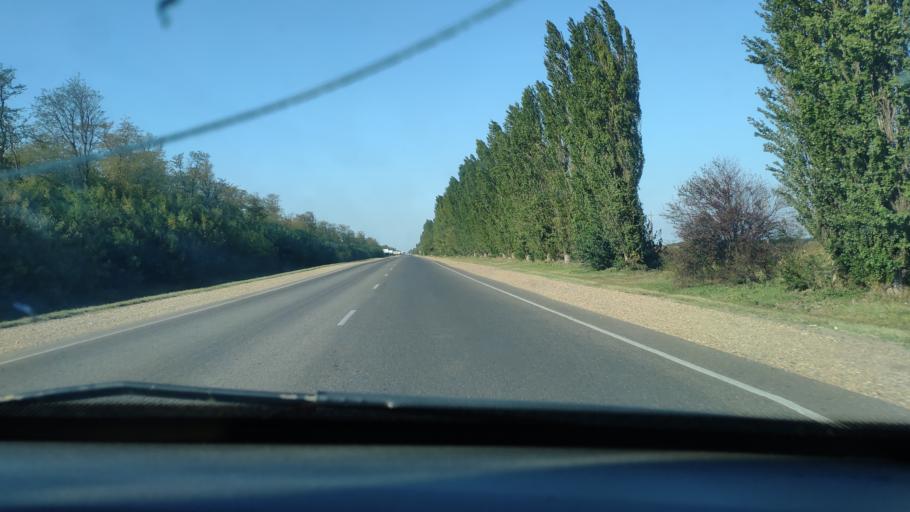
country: RU
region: Krasnodarskiy
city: Novotitarovskaya
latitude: 45.2680
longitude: 39.0029
